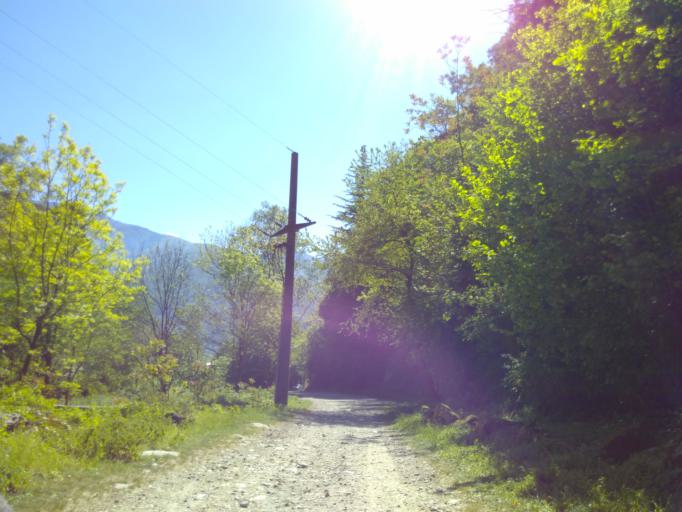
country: CH
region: Ticino
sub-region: Bellinzona District
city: Sementina
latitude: 46.1878
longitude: 8.9899
